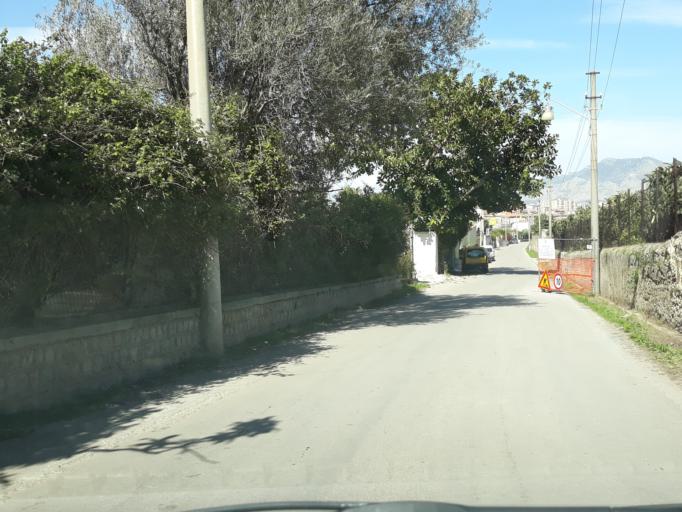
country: IT
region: Sicily
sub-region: Palermo
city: Villa Ciambra
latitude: 38.0769
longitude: 13.3470
